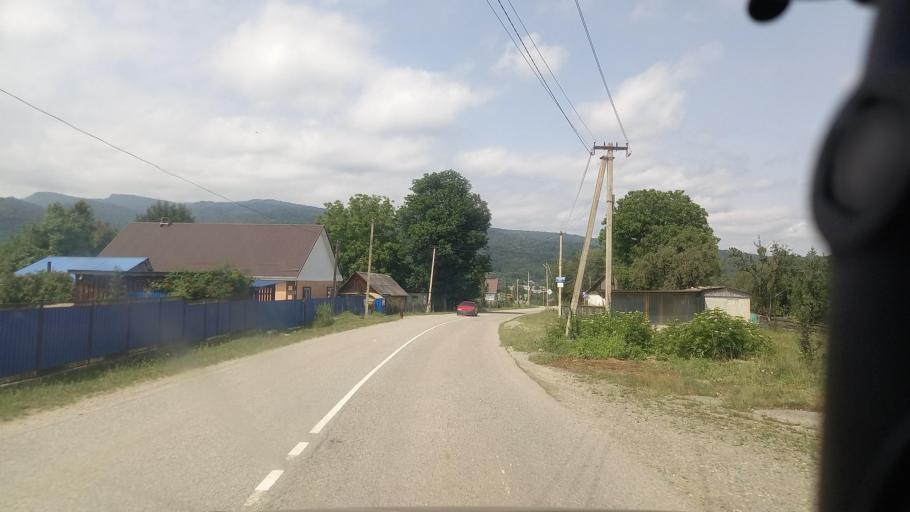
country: RU
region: Karachayevo-Cherkesiya
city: Kurdzhinovo
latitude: 43.9835
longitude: 40.9732
